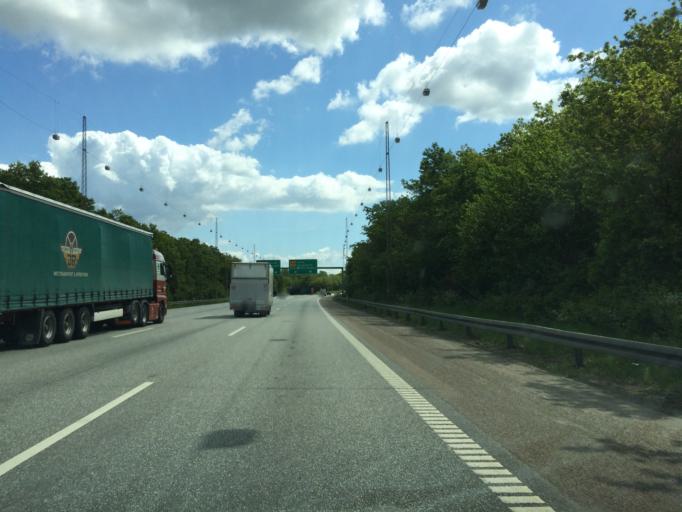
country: DK
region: Capital Region
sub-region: Hoje-Taastrup Kommune
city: Taastrup
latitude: 55.6647
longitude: 12.2975
